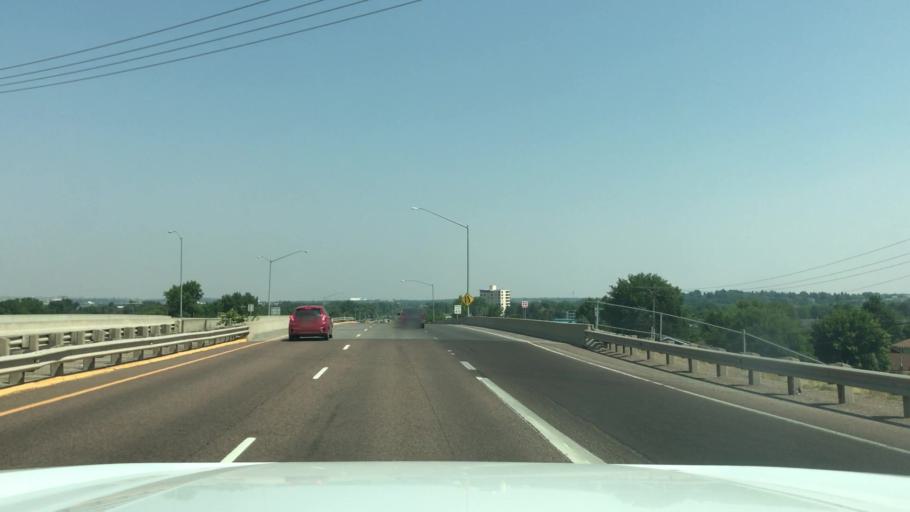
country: US
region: Montana
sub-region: Cascade County
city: Great Falls
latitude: 47.4876
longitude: -111.3360
